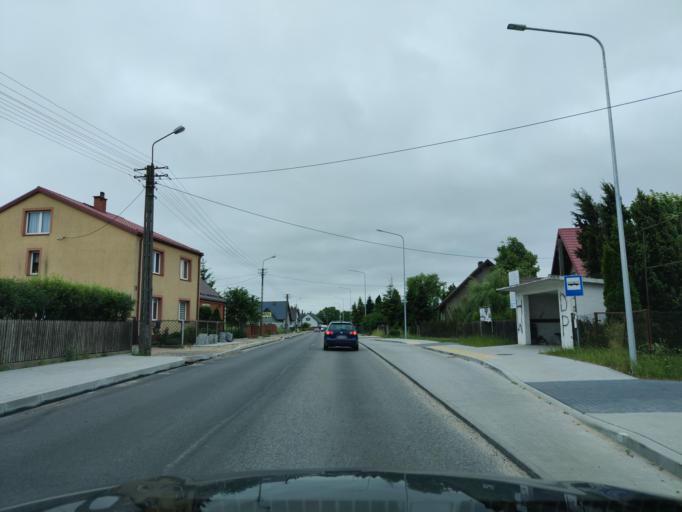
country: PL
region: Warmian-Masurian Voivodeship
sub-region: Powiat szczycienski
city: Rozogi
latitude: 53.4378
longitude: 21.3696
